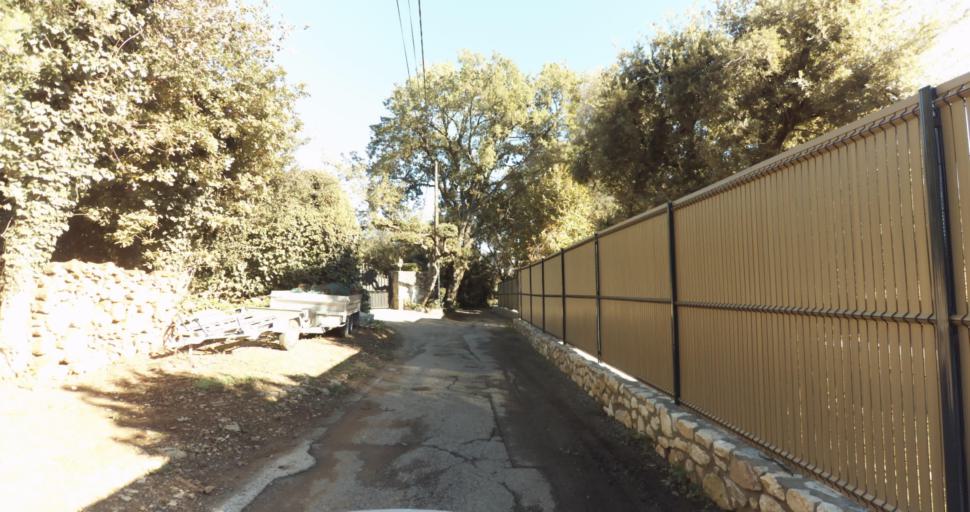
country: FR
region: Provence-Alpes-Cote d'Azur
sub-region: Departement des Alpes-Maritimes
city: Vence
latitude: 43.7134
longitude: 7.1030
